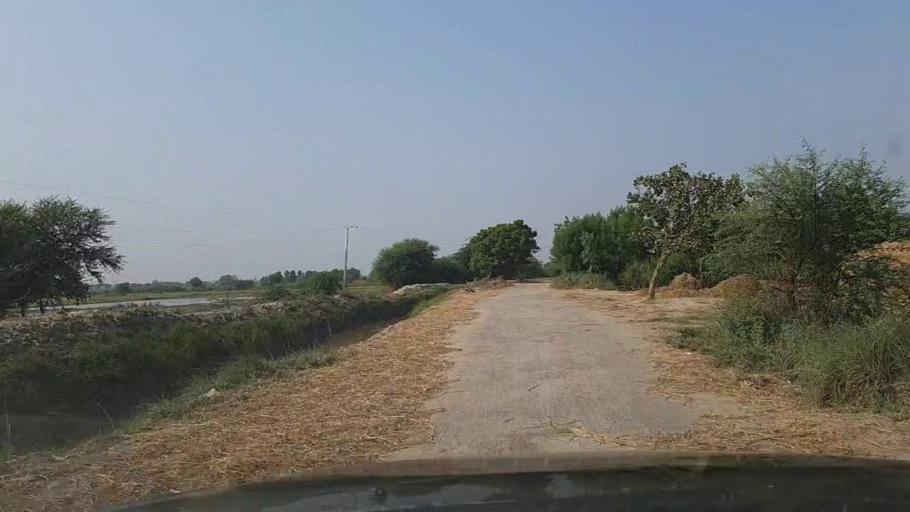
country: PK
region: Sindh
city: Mirpur Batoro
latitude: 24.7042
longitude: 68.2549
